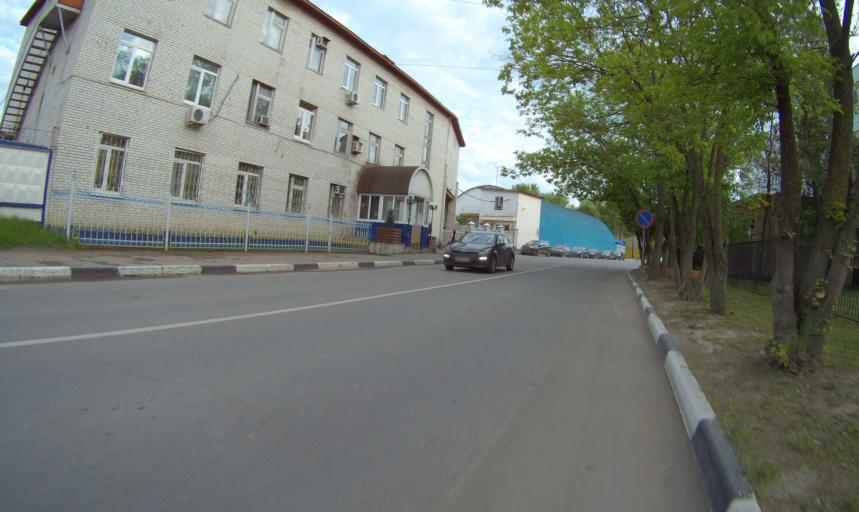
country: RU
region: Moskovskaya
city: Ramenskoye
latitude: 55.5716
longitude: 38.2465
